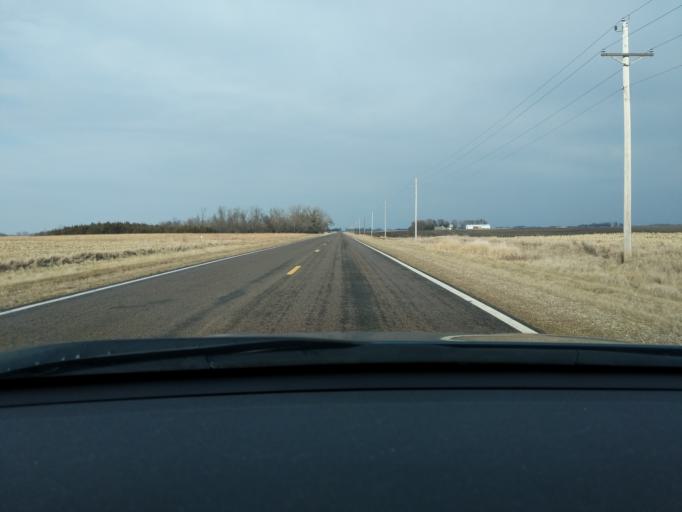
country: US
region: Minnesota
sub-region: Renville County
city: Renville
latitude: 44.7513
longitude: -95.3408
